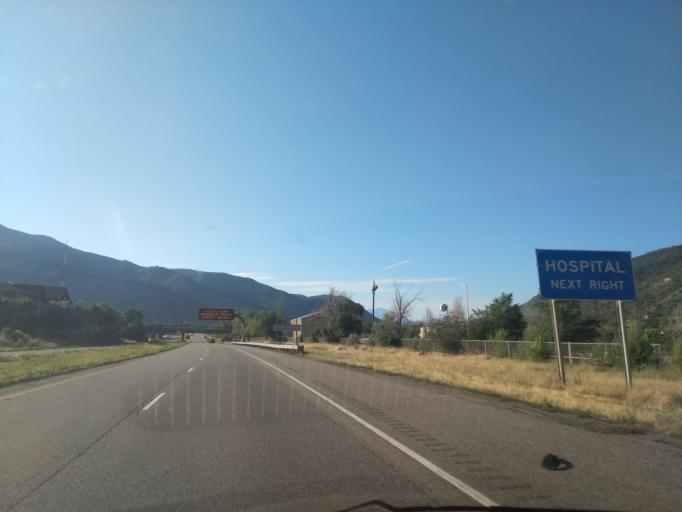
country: US
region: Colorado
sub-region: Garfield County
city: Glenwood Springs
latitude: 39.5550
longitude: -107.3352
